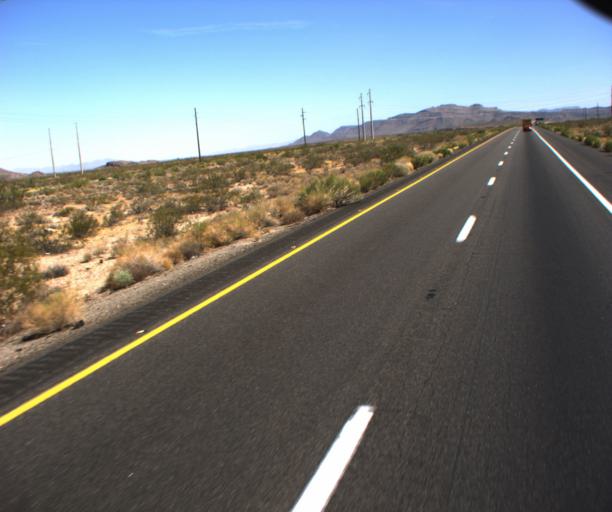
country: US
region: Arizona
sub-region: Mohave County
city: Kingman
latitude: 35.1012
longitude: -114.1175
